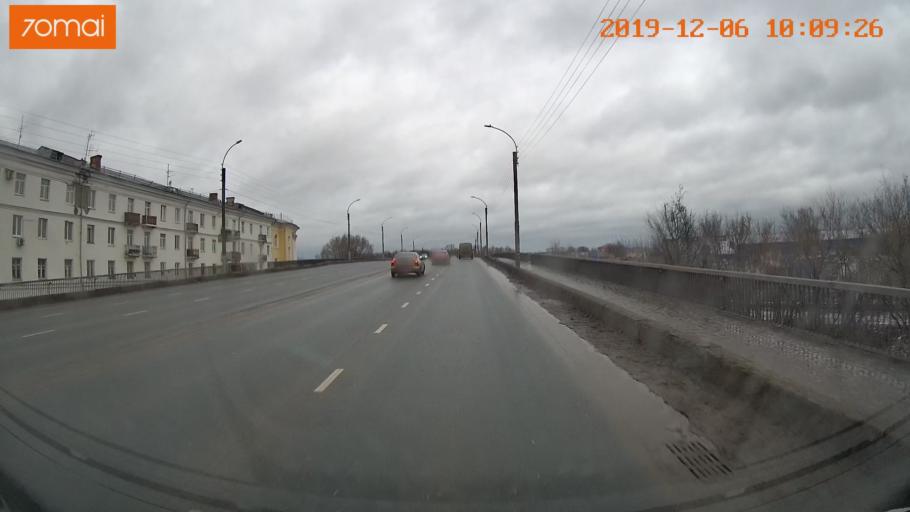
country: RU
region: Ivanovo
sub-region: Gorod Ivanovo
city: Ivanovo
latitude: 57.0234
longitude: 40.9674
